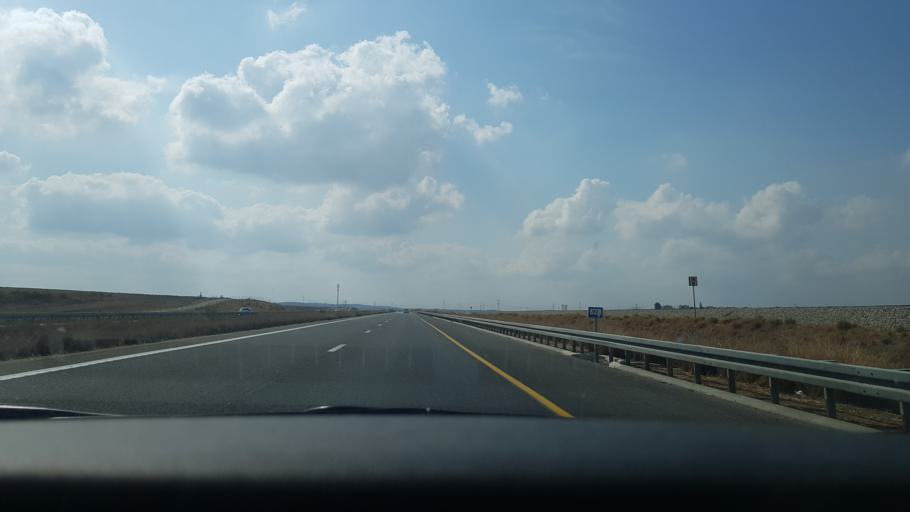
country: IL
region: Central District
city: Bene 'Ayish
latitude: 31.7304
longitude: 34.8212
